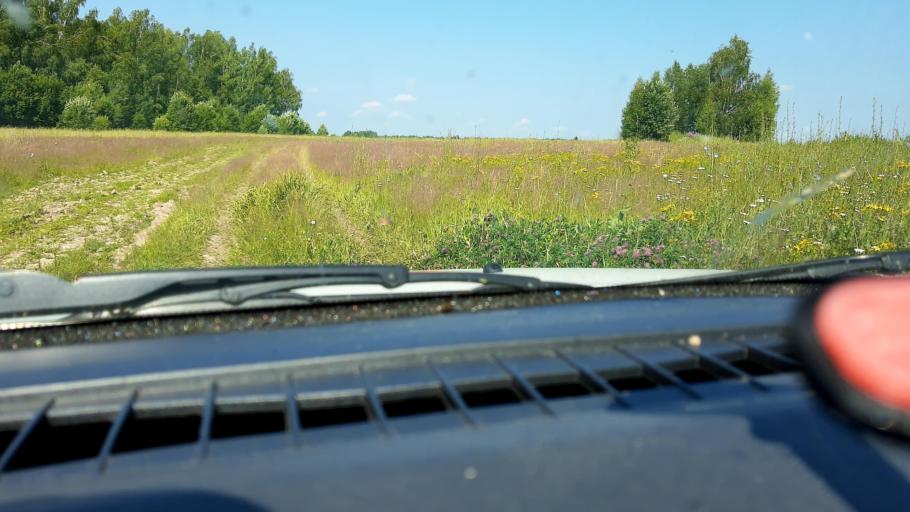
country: RU
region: Nizjnij Novgorod
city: Sharanga
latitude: 57.0461
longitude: 46.7239
